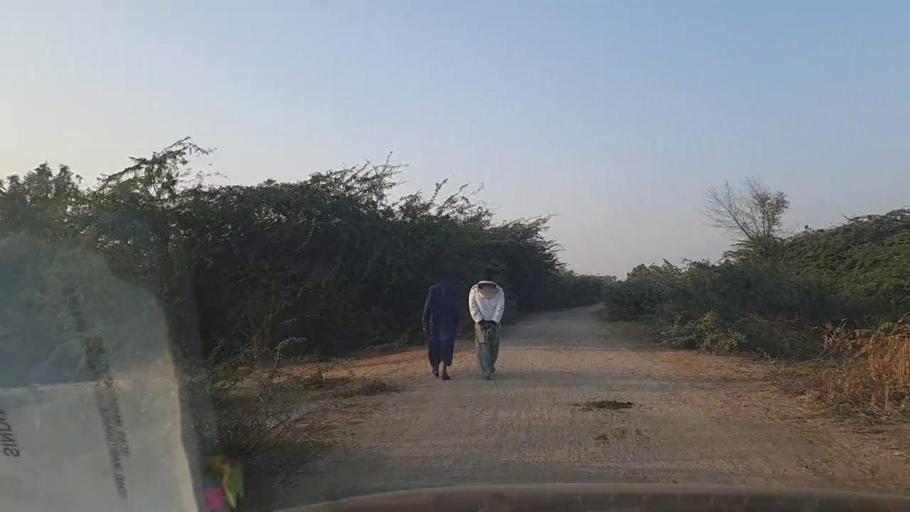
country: PK
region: Sindh
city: Keti Bandar
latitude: 24.3106
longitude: 67.6011
